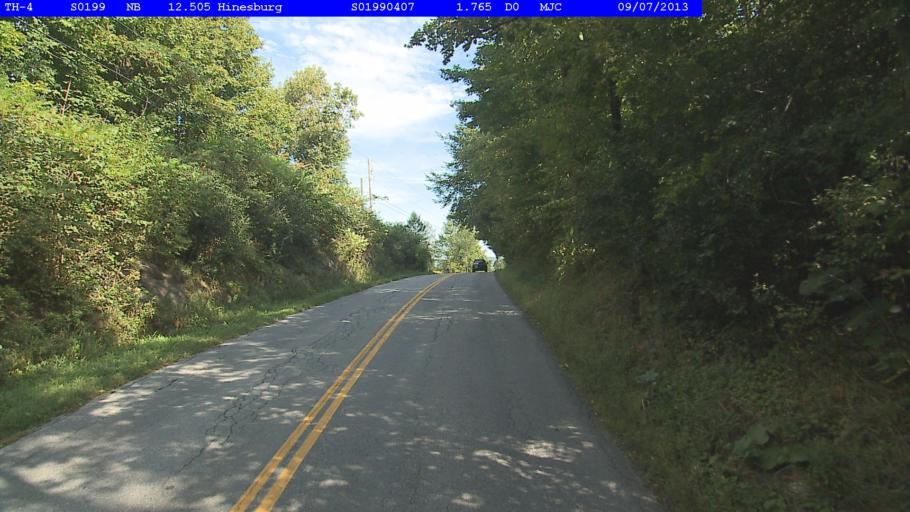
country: US
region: Vermont
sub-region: Chittenden County
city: Hinesburg
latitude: 44.3034
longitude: -73.1092
